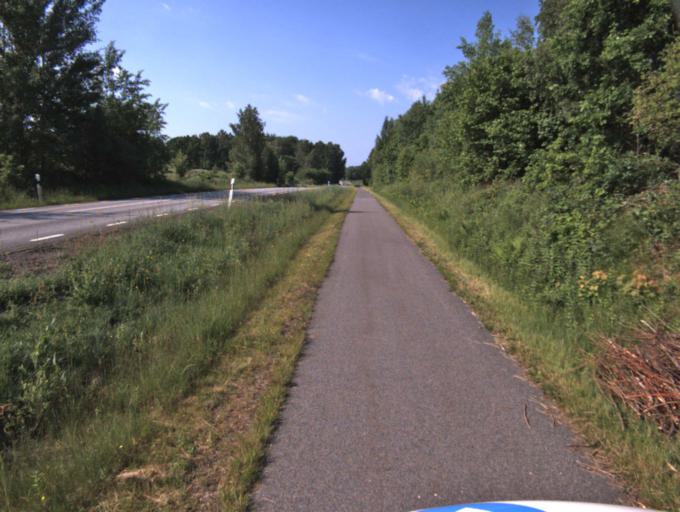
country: SE
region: Skane
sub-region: Kristianstads Kommun
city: Tollarp
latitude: 56.1631
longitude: 14.2763
